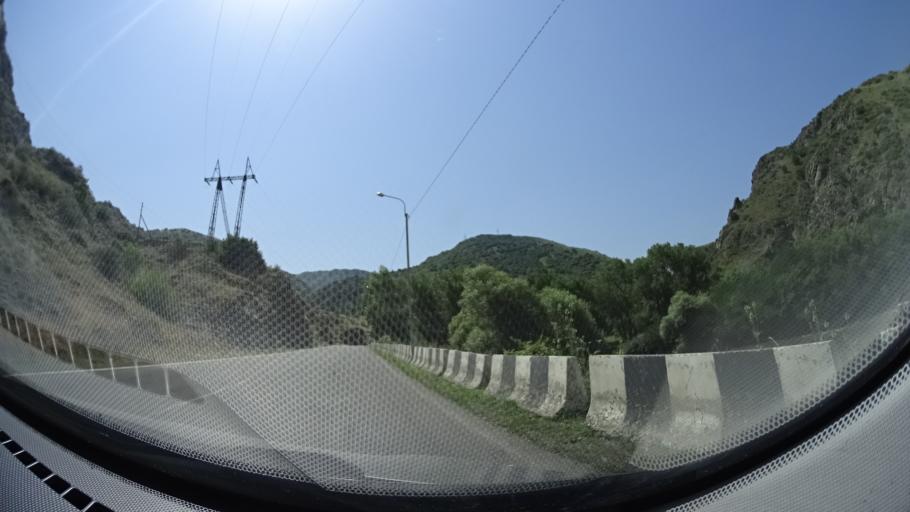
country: GE
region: Samtskhe-Javakheti
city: Aspindza
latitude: 41.5626
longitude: 43.2710
